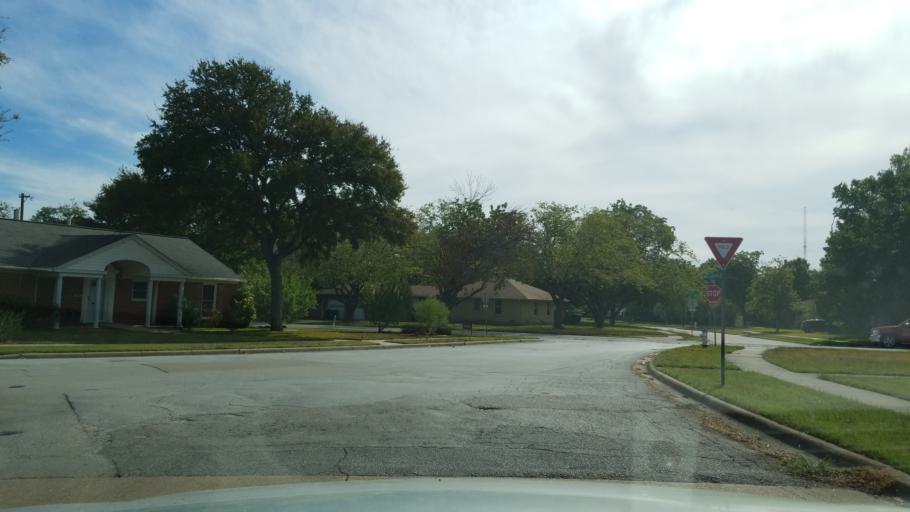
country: US
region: Texas
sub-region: Dallas County
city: Garland
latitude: 32.8975
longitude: -96.6531
